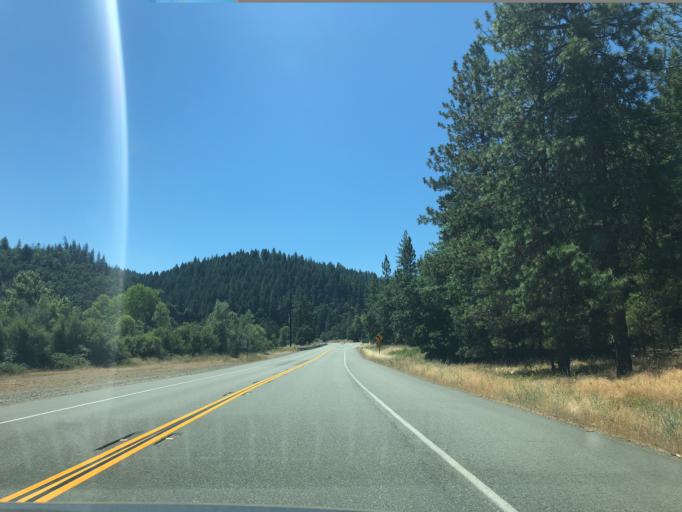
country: US
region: California
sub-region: Trinity County
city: Weaverville
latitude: 40.6563
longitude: -122.9428
